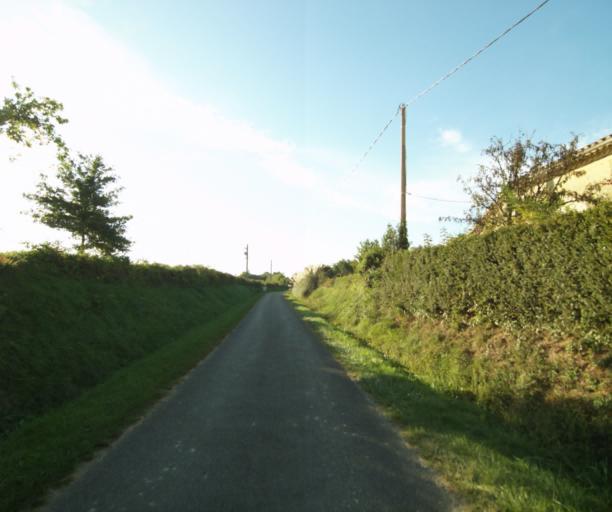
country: FR
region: Midi-Pyrenees
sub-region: Departement du Gers
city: Cazaubon
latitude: 43.8695
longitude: 0.0012
